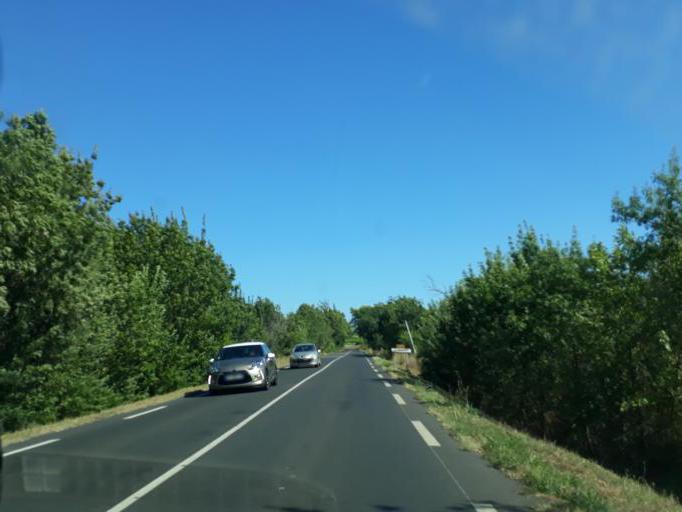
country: FR
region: Languedoc-Roussillon
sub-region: Departement de l'Herault
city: Florensac
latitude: 43.3779
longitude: 3.4714
